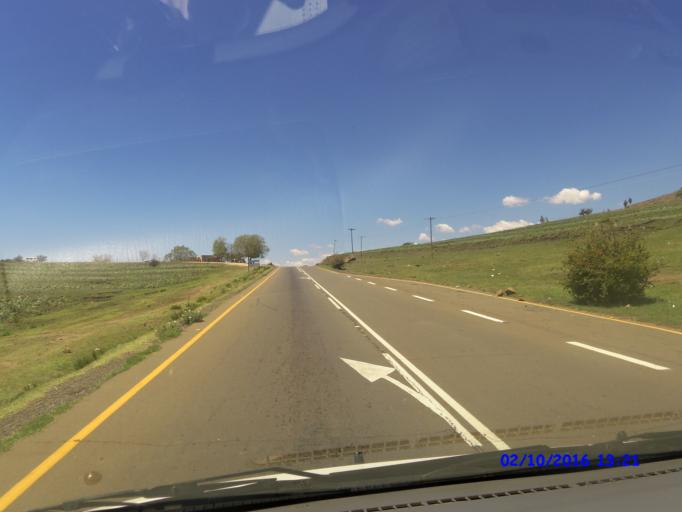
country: LS
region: Maseru
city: Nako
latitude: -29.4193
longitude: 27.7119
